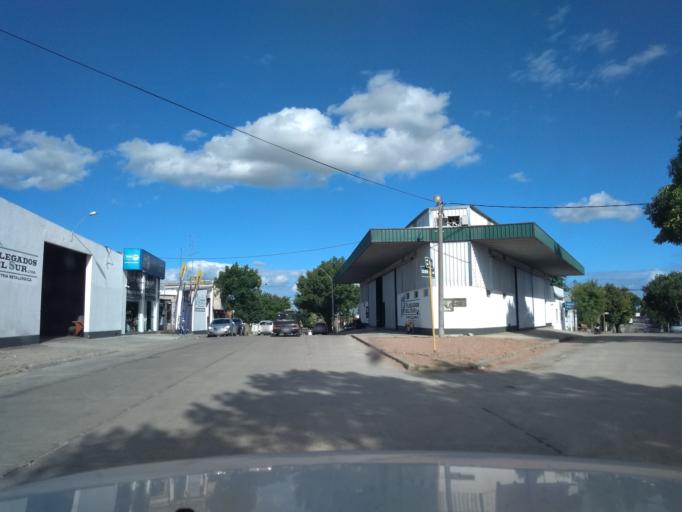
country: UY
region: Florida
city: Florida
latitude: -34.0907
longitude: -56.2186
